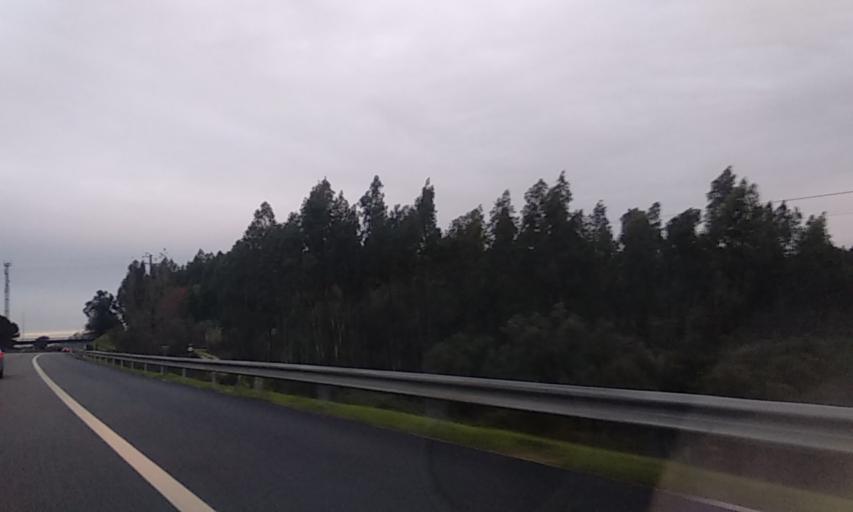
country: PT
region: Aveiro
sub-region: Mealhada
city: Mealhada
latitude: 40.3407
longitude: -8.4955
